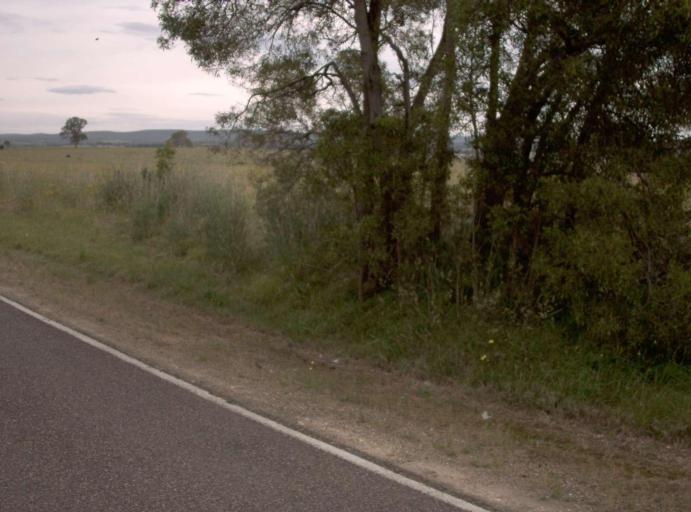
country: AU
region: Victoria
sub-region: East Gippsland
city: Bairnsdale
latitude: -37.8236
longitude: 147.5058
